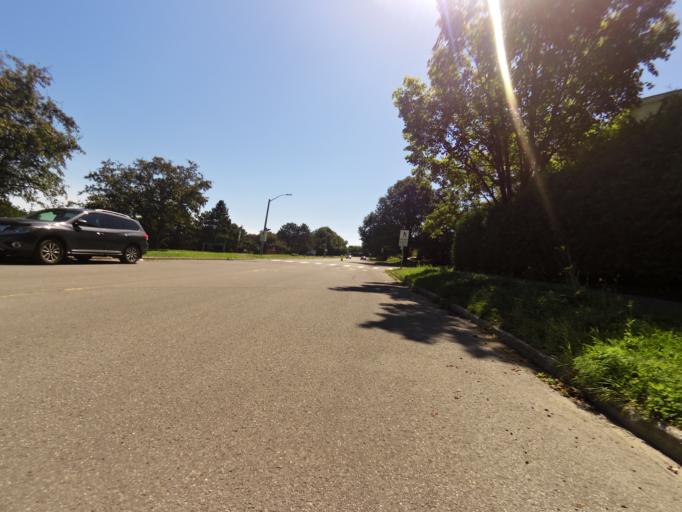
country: CA
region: Ontario
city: Ottawa
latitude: 45.3538
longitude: -75.6655
